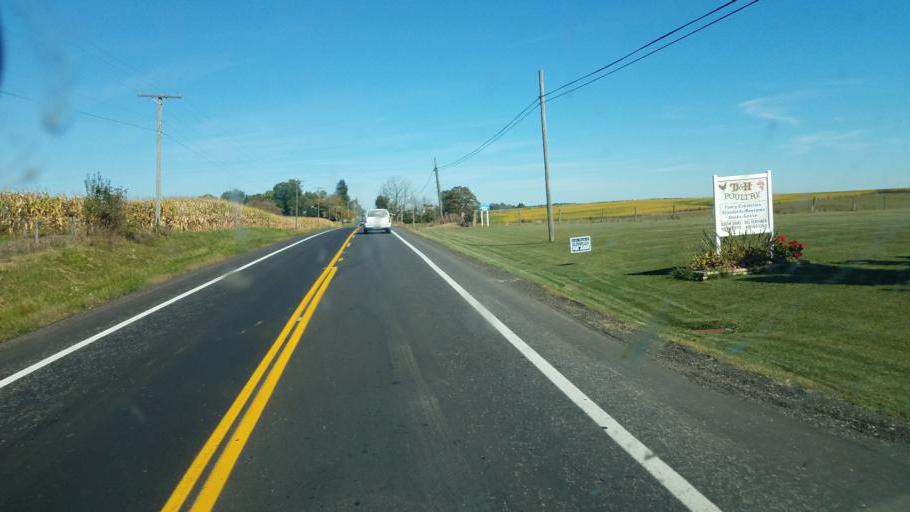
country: US
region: Ohio
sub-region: Richland County
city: Lexington
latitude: 40.6115
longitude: -82.6627
